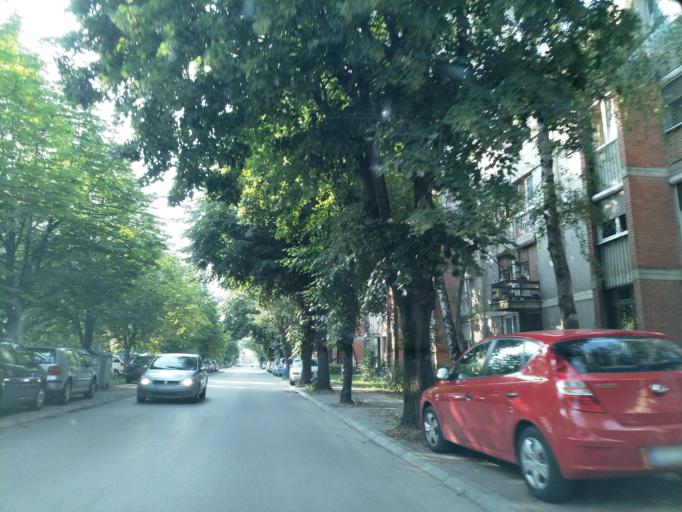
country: RS
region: Central Serbia
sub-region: Pomoravski Okrug
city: Jagodina
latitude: 43.9784
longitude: 21.2480
